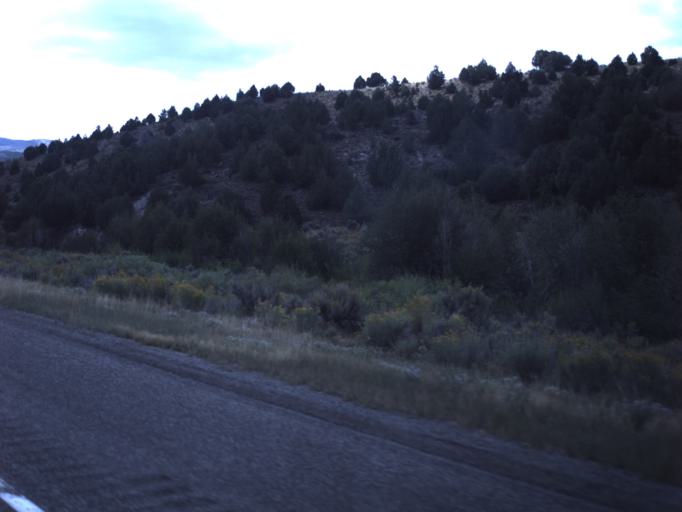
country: US
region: Utah
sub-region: Sevier County
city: Salina
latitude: 38.8462
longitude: -111.5400
